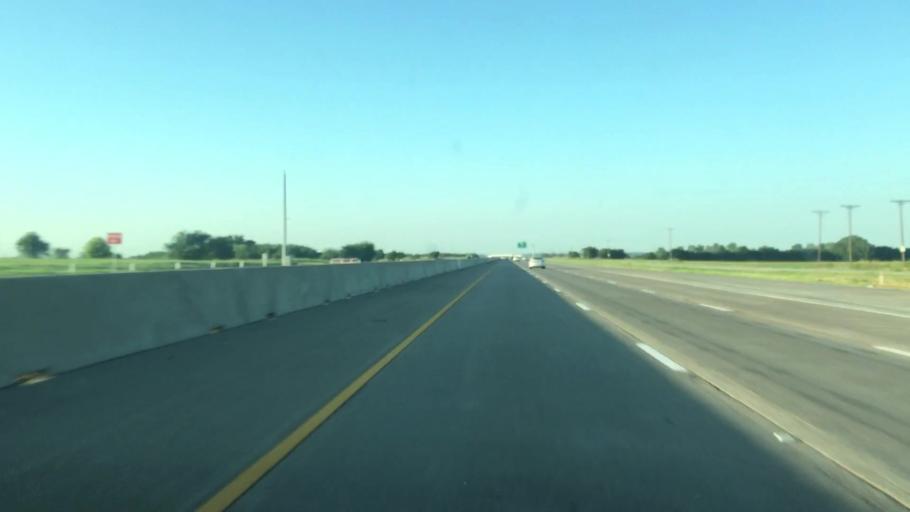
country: US
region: Texas
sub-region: Ellis County
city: Nash
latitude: 32.2821
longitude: -96.8682
